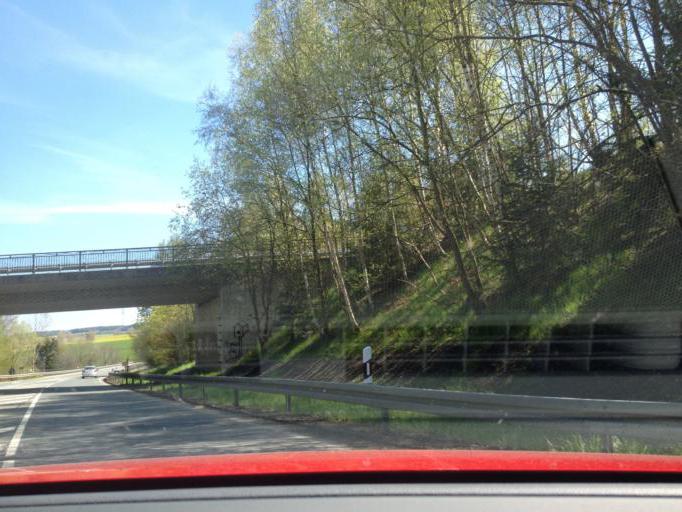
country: DE
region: Bavaria
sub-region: Upper Franconia
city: Schwarzenbach an der Saale
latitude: 50.2290
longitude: 11.9312
